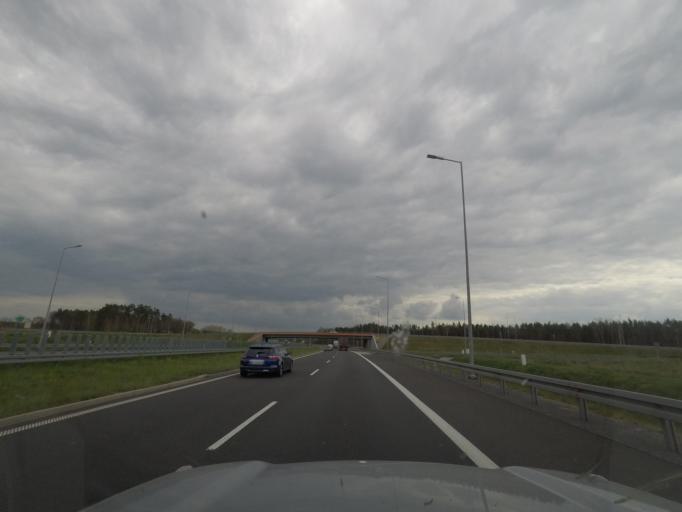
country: PL
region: Lubusz
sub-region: Powiat nowosolski
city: Nowe Miasteczko
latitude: 51.6837
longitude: 15.7596
